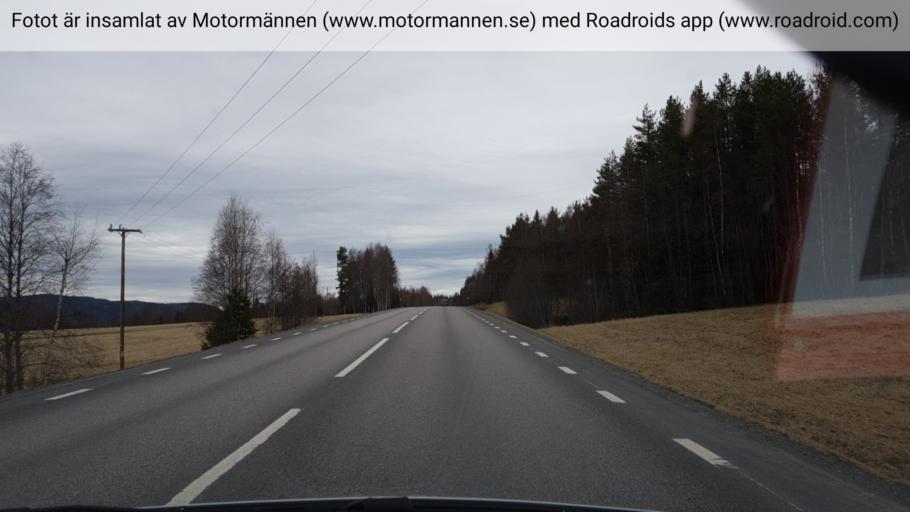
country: SE
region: Vaesternorrland
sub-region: Solleftea Kommun
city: Solleftea
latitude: 63.1846
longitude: 17.2471
